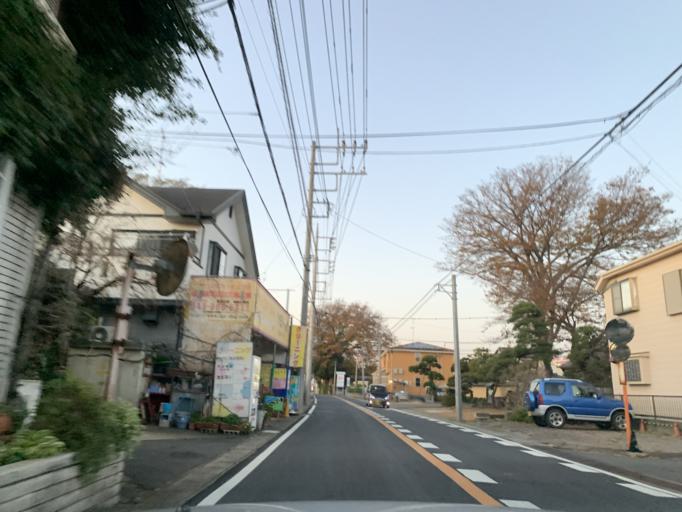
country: JP
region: Chiba
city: Nagareyama
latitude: 35.9047
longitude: 139.9050
